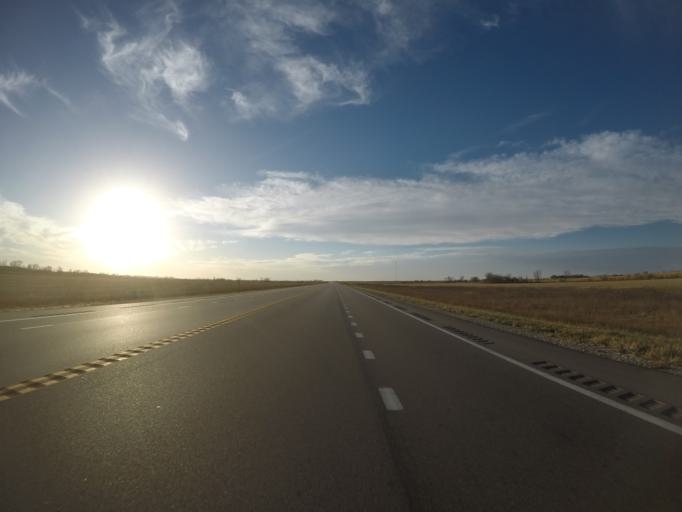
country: US
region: Kansas
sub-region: Chase County
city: Cottonwood Falls
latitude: 38.4048
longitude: -96.3965
